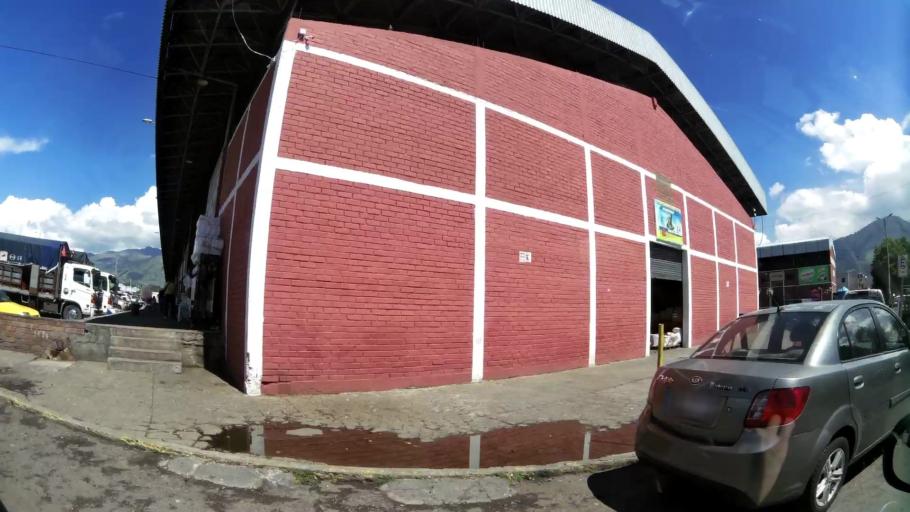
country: EC
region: Pichincha
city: Quito
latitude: -0.2700
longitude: -78.5340
